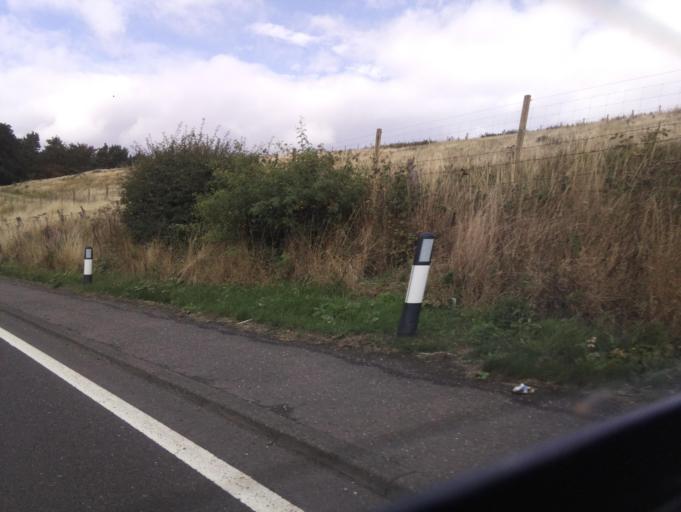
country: GB
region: Scotland
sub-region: East Lothian
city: Pencaitland
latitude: 55.8389
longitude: -2.9082
